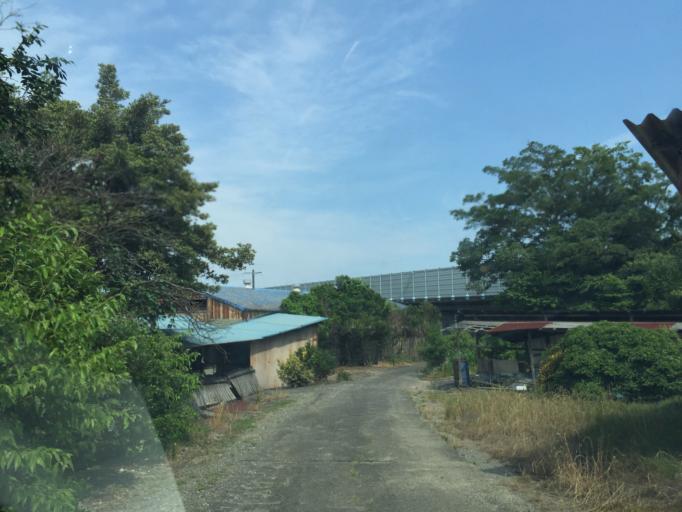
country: JP
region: Shizuoka
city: Fukuroi
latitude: 34.7683
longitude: 137.9597
